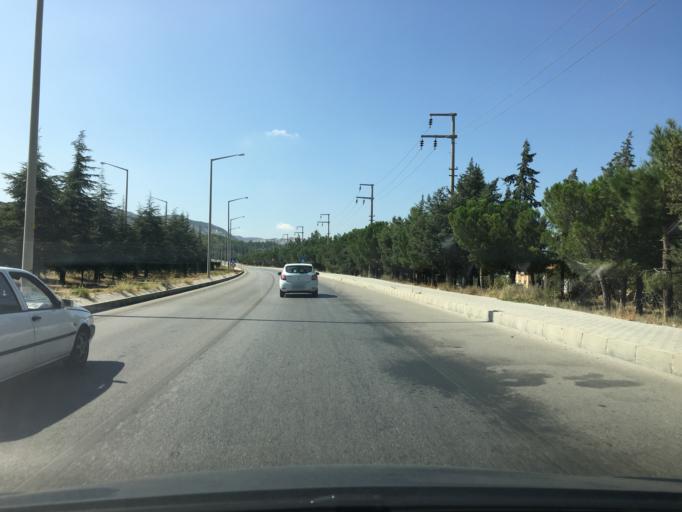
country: TR
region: Burdur
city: Burdur
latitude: 37.7260
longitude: 30.3004
